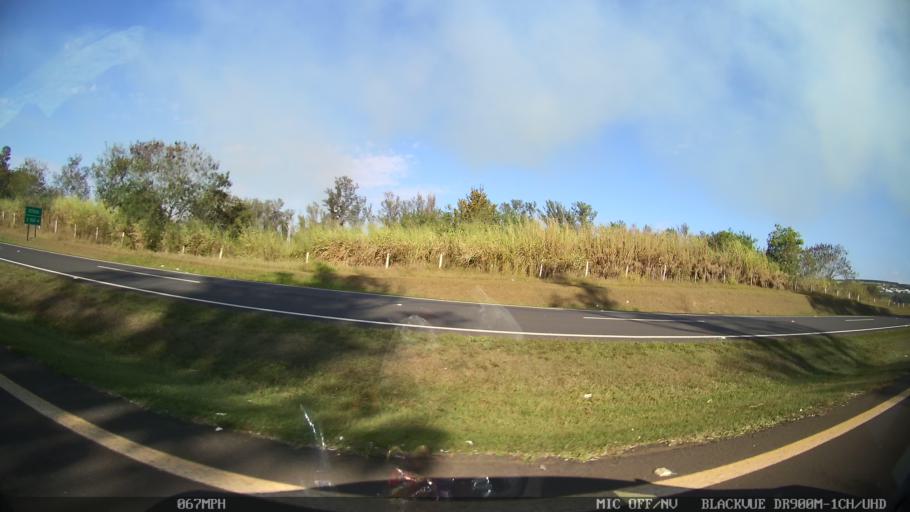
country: BR
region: Sao Paulo
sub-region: Piracicaba
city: Piracicaba
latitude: -22.6917
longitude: -47.5882
